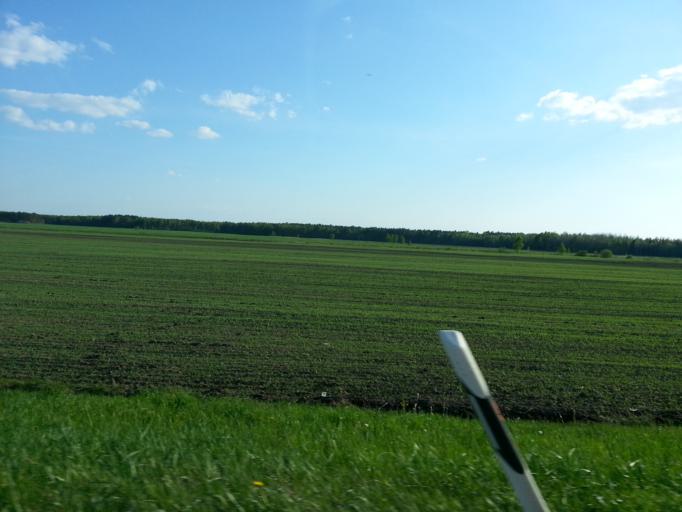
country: LT
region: Panevezys
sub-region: Panevezys City
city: Panevezys
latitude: 55.6739
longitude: 24.3334
